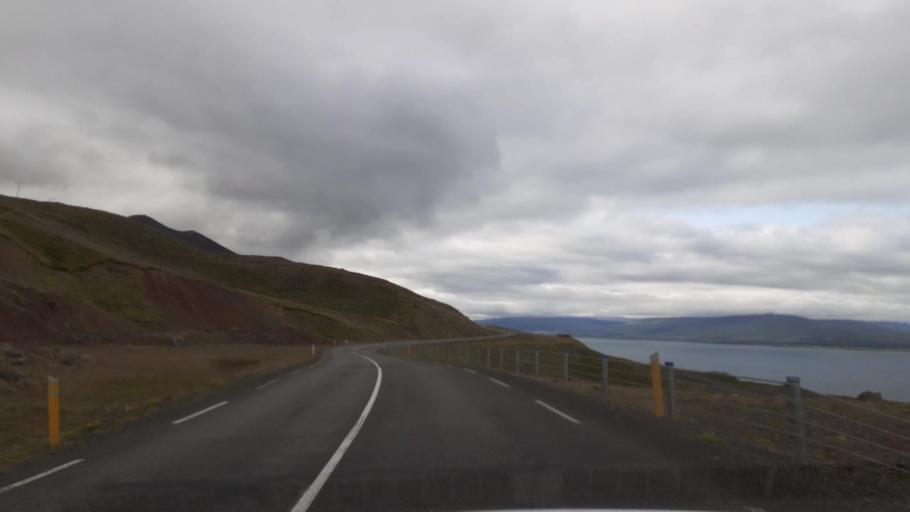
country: IS
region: Northeast
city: Akureyri
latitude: 65.8346
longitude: -18.0560
